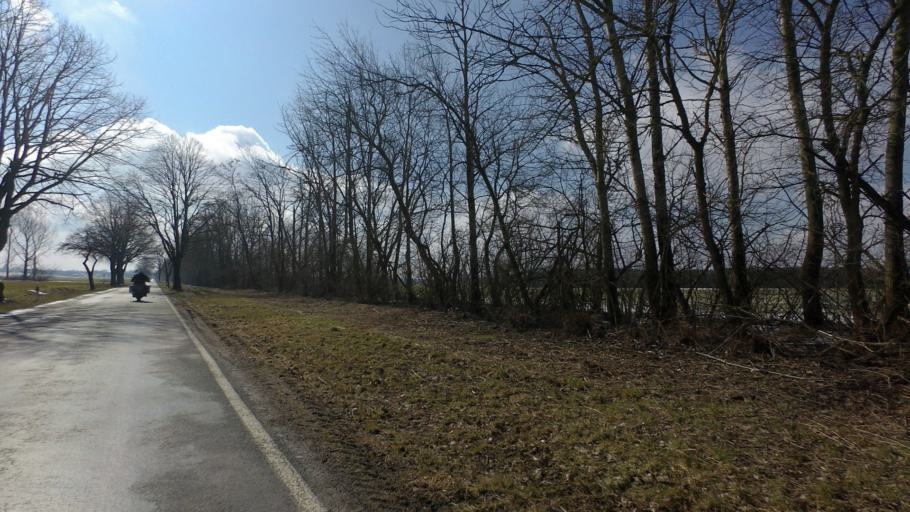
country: DE
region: Brandenburg
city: Werneuchen
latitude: 52.6964
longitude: 13.7226
